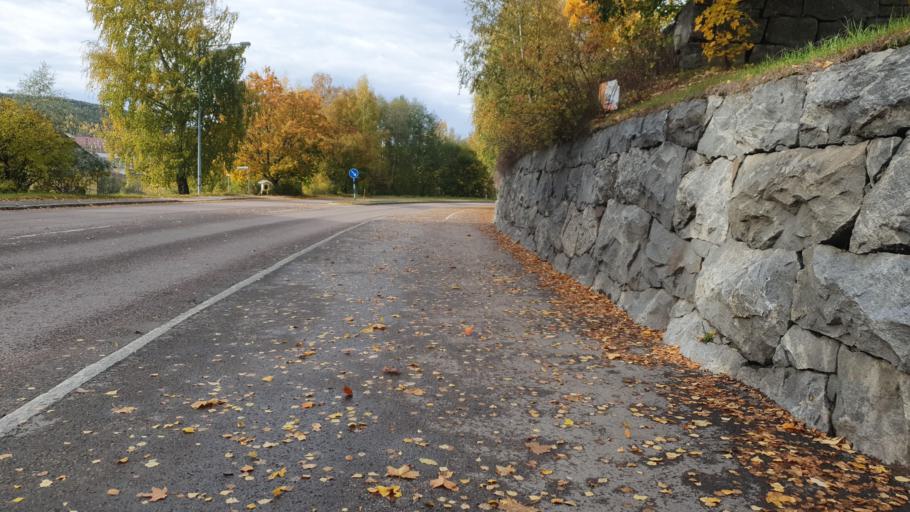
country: SE
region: Vaesternorrland
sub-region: Sundsvalls Kommun
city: Sundsvall
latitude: 62.3943
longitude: 17.2750
